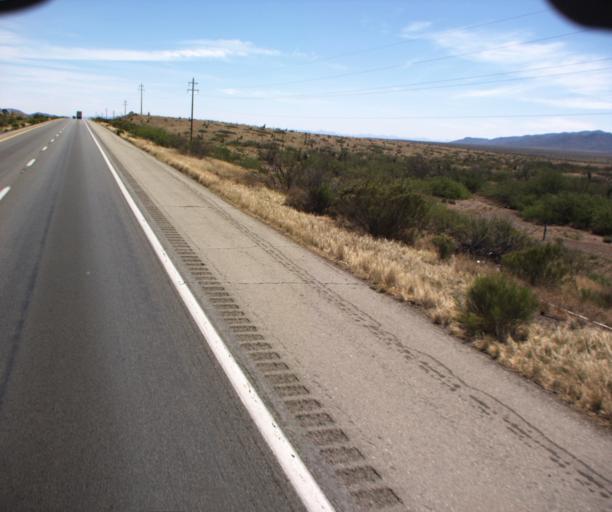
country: US
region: Arizona
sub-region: Cochise County
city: Willcox
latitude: 32.3537
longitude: -109.7130
